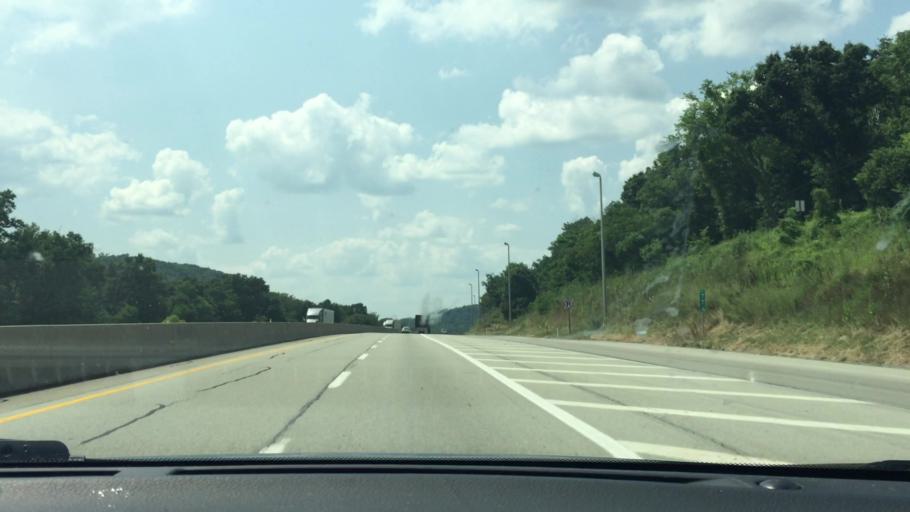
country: US
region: Pennsylvania
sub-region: Westmoreland County
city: Youngwood
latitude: 40.2066
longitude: -79.5697
